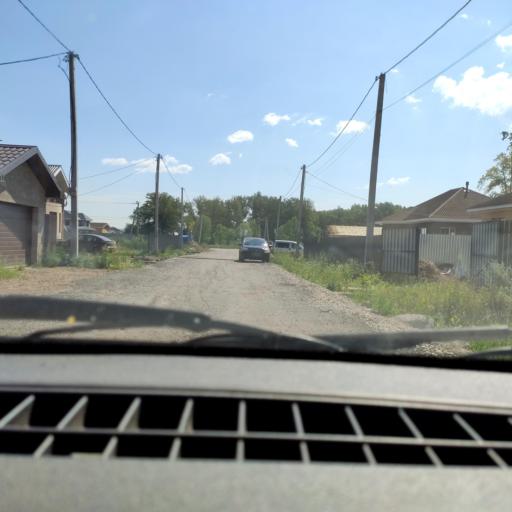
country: RU
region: Bashkortostan
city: Mikhaylovka
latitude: 54.8137
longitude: 55.9333
